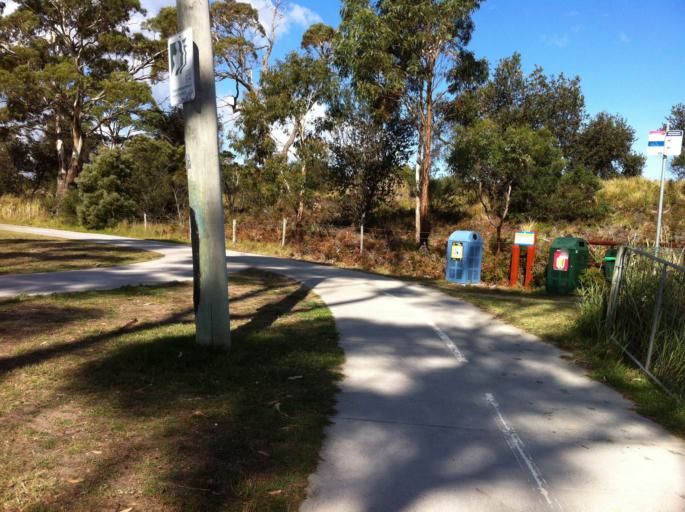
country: AU
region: Tasmania
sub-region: Clarence
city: Bellerive
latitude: -42.8784
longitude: 147.3786
